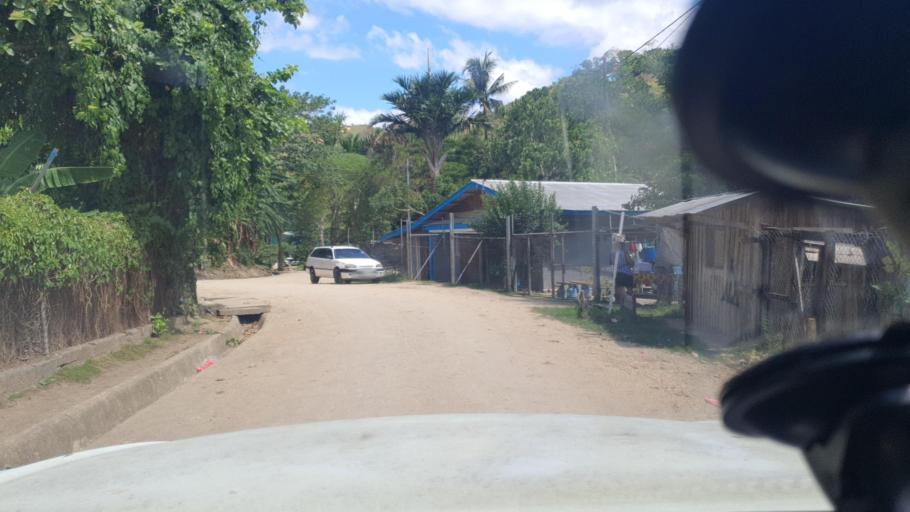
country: SB
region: Guadalcanal
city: Honiara
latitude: -9.4457
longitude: 159.9595
